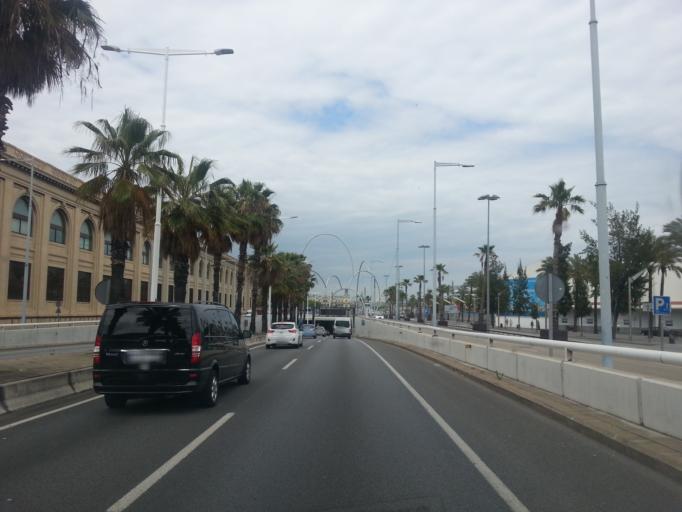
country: ES
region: Catalonia
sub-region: Provincia de Barcelona
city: Ciutat Vella
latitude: 41.3712
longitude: 2.1752
